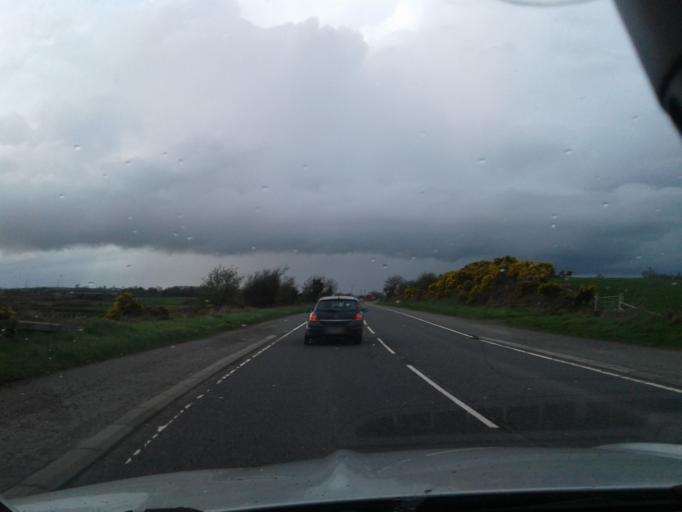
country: GB
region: Northern Ireland
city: Newtownstewart
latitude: 54.7366
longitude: -7.4330
